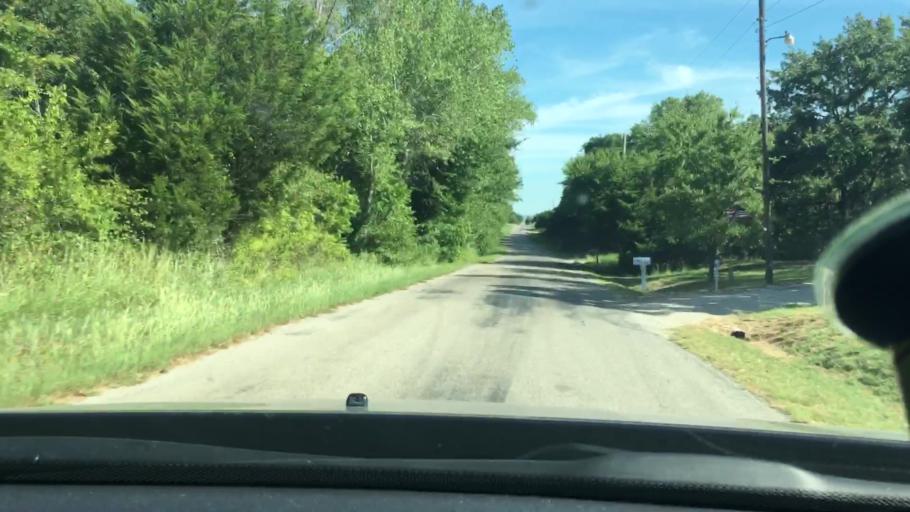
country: US
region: Oklahoma
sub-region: Carter County
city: Lone Grove
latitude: 34.2538
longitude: -97.2474
